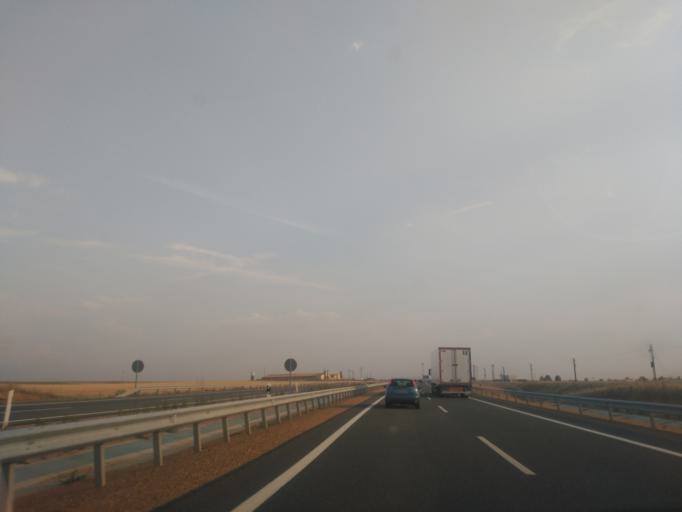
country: ES
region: Castille and Leon
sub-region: Provincia de Zamora
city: Montamarta
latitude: 41.6494
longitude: -5.7942
